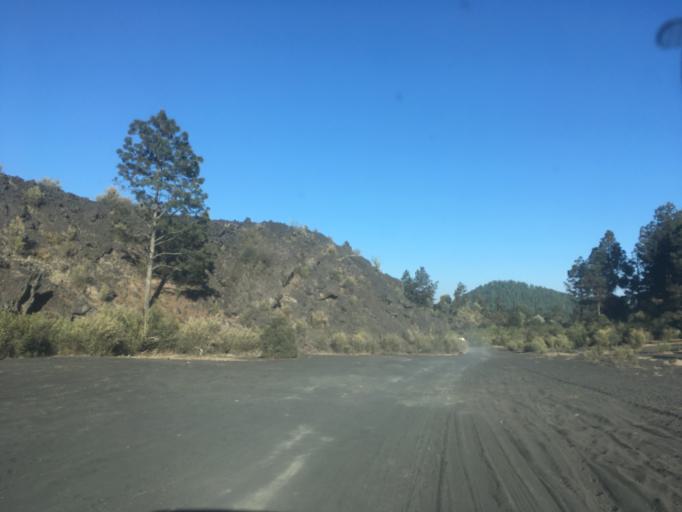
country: MX
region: Michoacan
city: Angahuan
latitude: 19.4820
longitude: -102.2519
